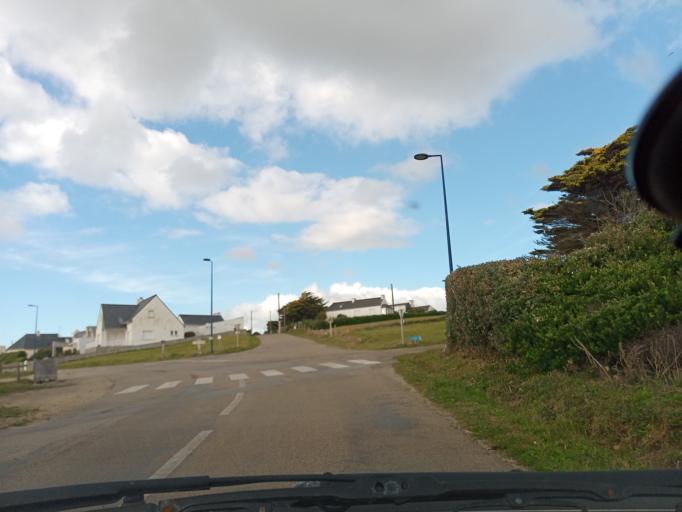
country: FR
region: Brittany
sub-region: Departement du Finistere
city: Plozevet
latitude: 47.9809
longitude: -4.4497
